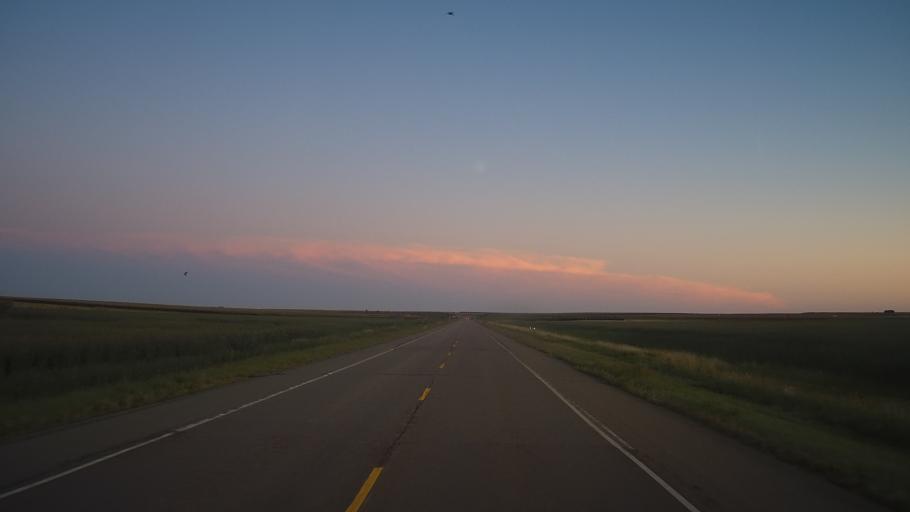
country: US
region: South Dakota
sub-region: Lyman County
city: Kennebec
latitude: 43.8725
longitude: -99.6060
